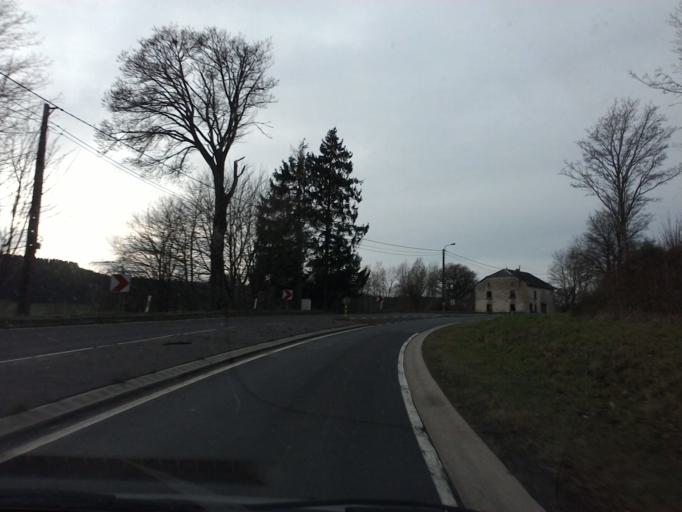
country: BE
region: Wallonia
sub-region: Province de Liege
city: Lierneux
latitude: 50.2615
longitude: 5.8403
